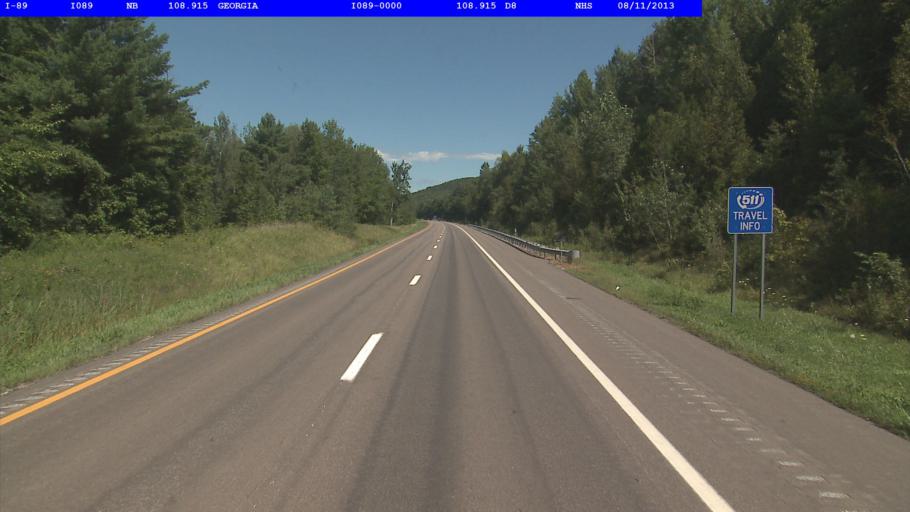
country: US
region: Vermont
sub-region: Franklin County
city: Saint Albans
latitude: 44.7255
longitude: -73.0813
